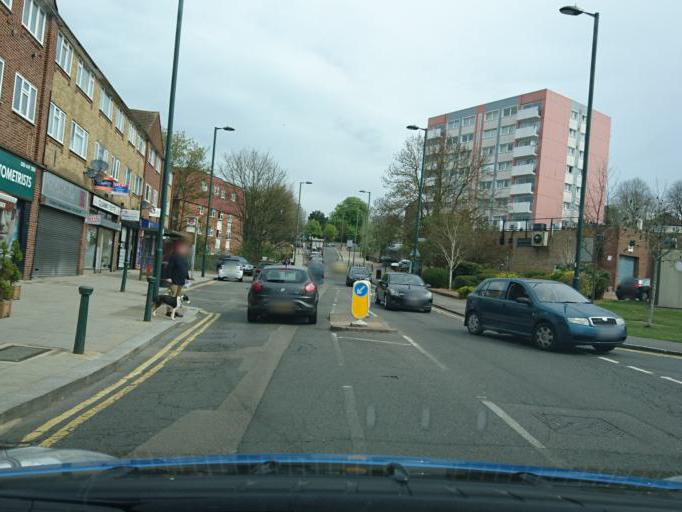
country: GB
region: England
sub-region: Greater London
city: Hadley Wood
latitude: 51.6429
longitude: -0.1623
